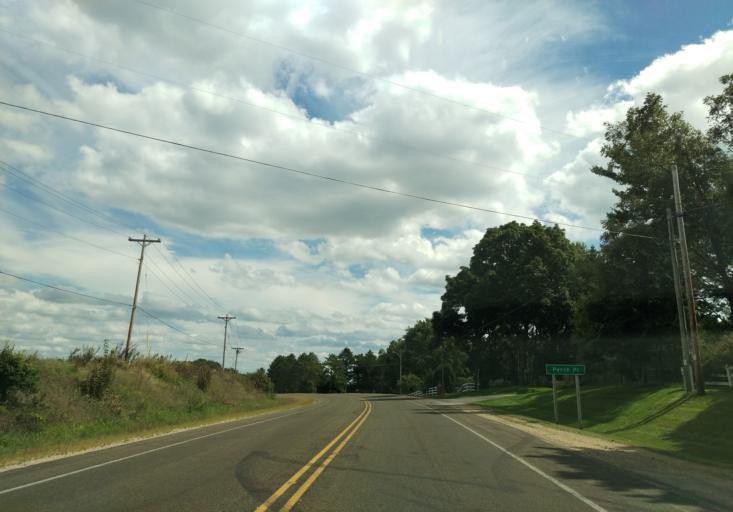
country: US
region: Wisconsin
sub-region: Dane County
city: Shorewood Hills
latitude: 43.1191
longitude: -89.4462
